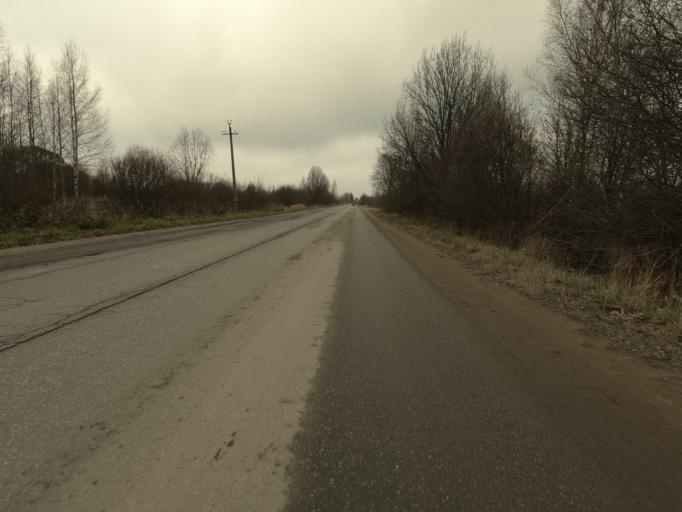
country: RU
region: Leningrad
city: Lyuban'
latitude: 59.4824
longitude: 31.2630
